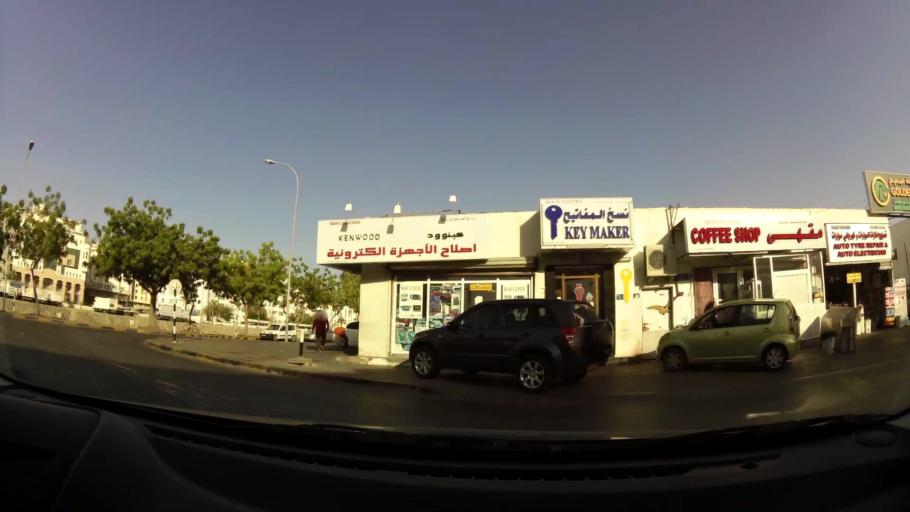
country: OM
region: Muhafazat Masqat
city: Muscat
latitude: 23.5918
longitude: 58.5491
